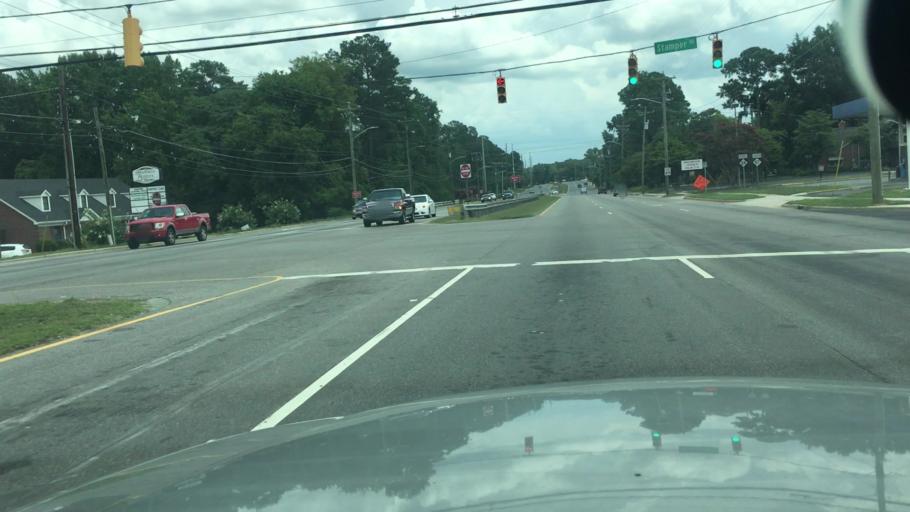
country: US
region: North Carolina
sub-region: Cumberland County
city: Fayetteville
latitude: 35.0722
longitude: -78.9234
